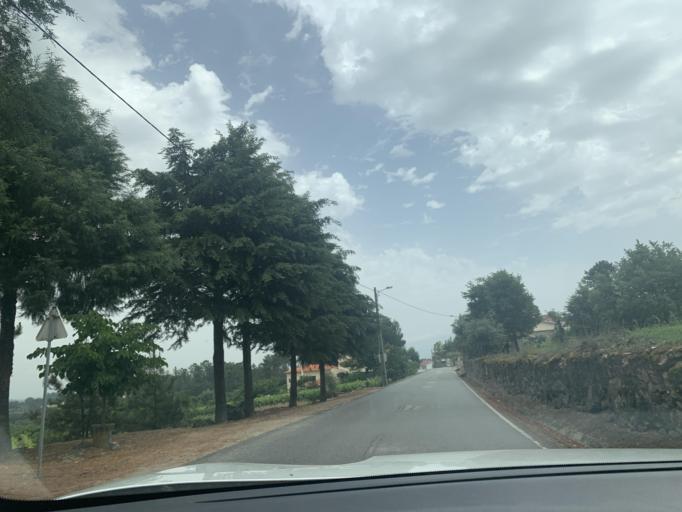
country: PT
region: Viseu
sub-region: Mangualde
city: Mangualde
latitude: 40.5622
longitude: -7.6967
